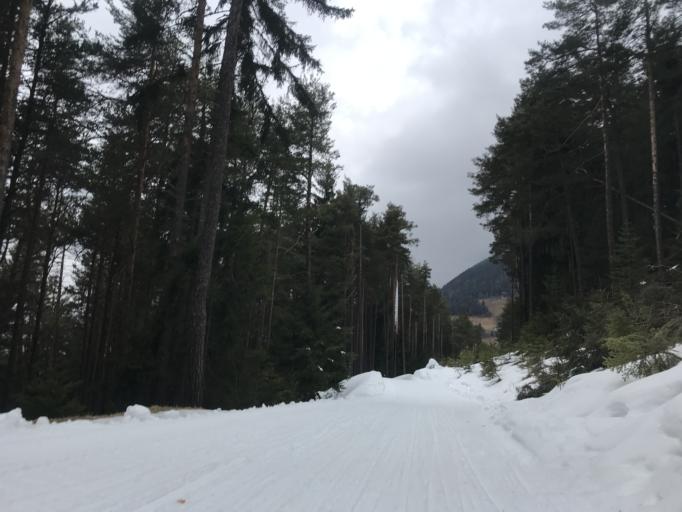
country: IT
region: Trentino-Alto Adige
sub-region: Bolzano
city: Bressanone
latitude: 46.6881
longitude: 11.6850
